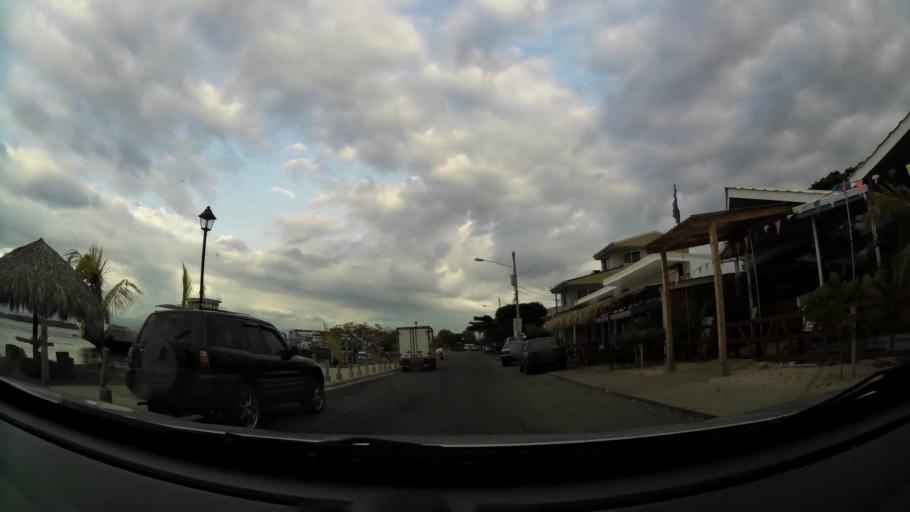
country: CR
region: Puntarenas
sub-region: Canton Central de Puntarenas
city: Puntarenas
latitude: 9.9774
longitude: -84.8501
